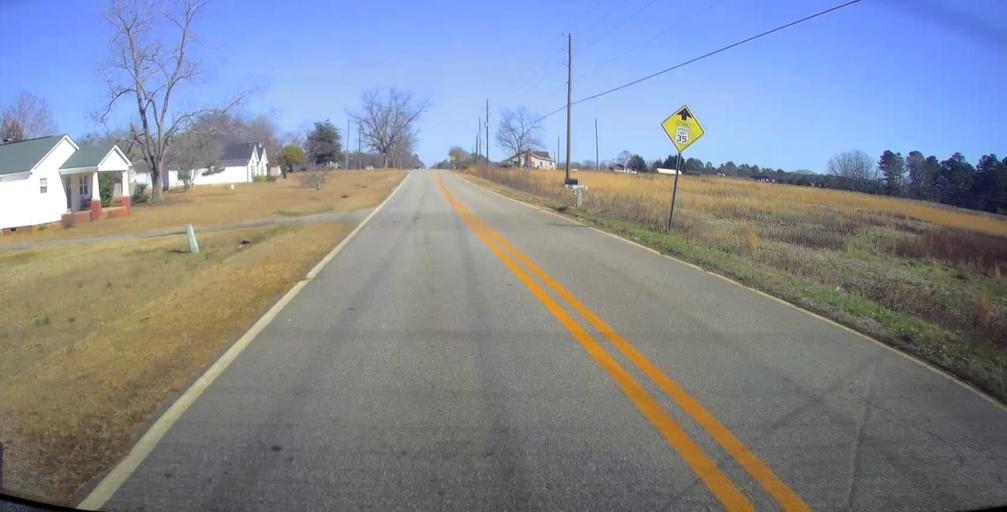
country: US
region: Georgia
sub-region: Peach County
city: Byron
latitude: 32.6191
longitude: -83.7721
